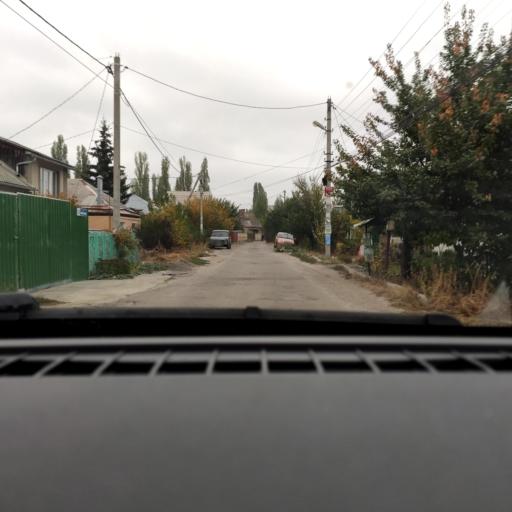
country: RU
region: Voronezj
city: Voronezh
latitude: 51.6732
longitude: 39.2652
